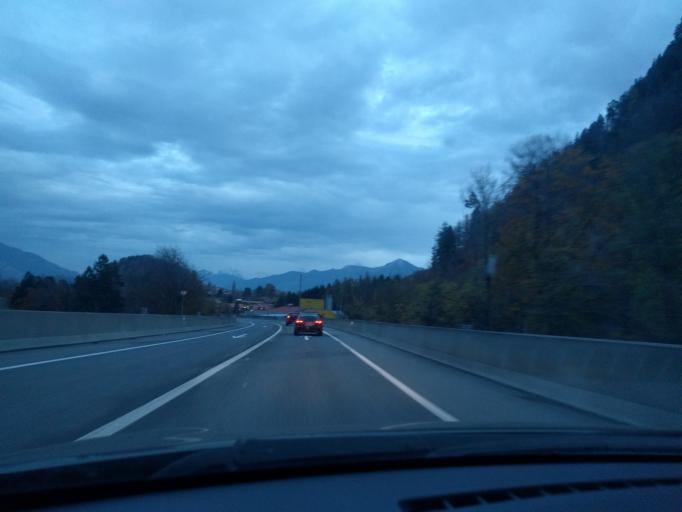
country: CH
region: Bern
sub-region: Frutigen-Niedersimmental District
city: Wimmis
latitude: 46.6752
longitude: 7.6279
